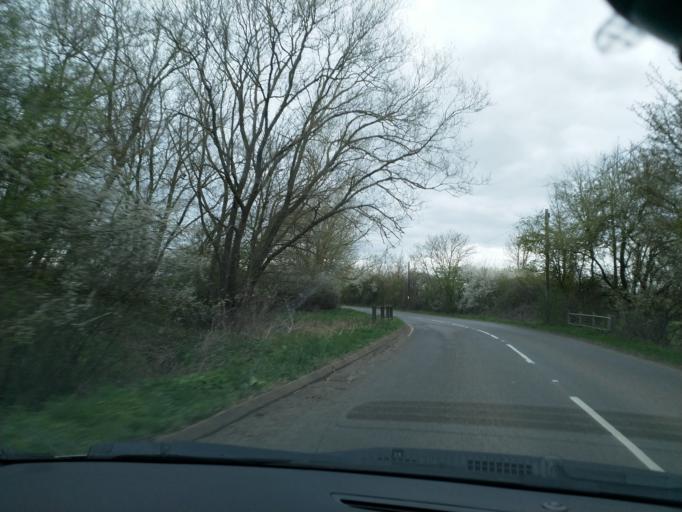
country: GB
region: England
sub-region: Warwickshire
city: Harbury
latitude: 52.1485
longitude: -1.4730
